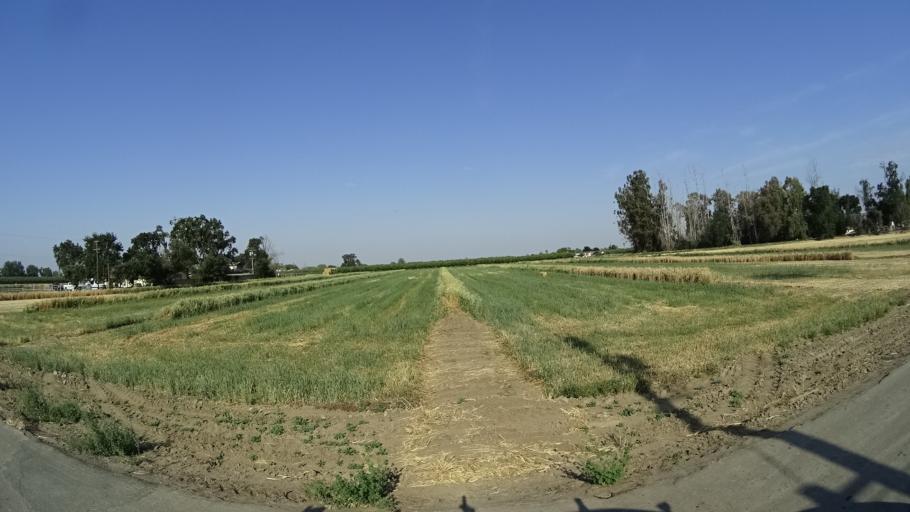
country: US
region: California
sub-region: Fresno County
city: Riverdale
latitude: 36.3680
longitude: -119.8250
